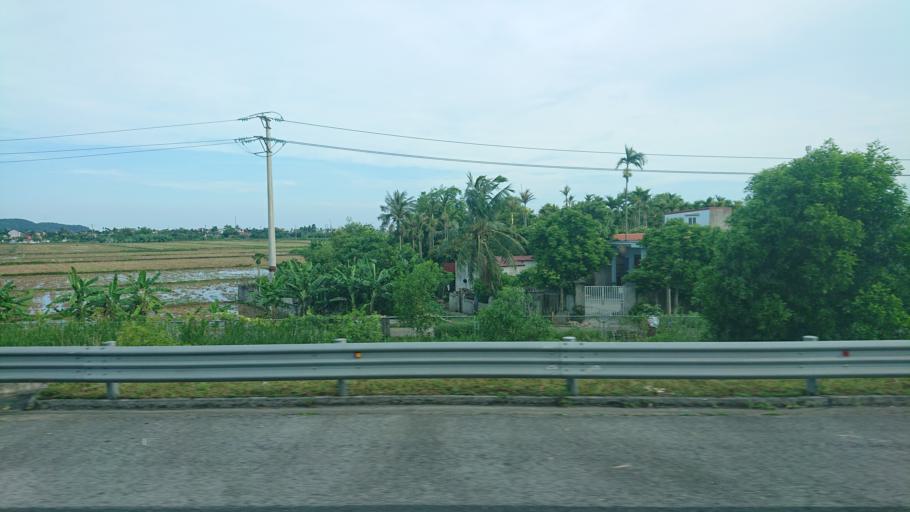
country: VN
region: Hai Phong
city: Nui Doi
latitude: 20.7660
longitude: 106.6471
